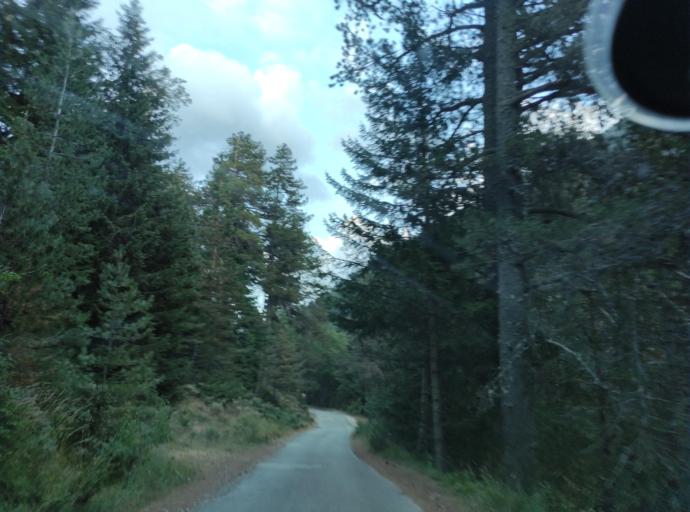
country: BG
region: Blagoevgrad
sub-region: Obshtina Bansko
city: Bansko
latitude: 41.7675
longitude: 23.4252
